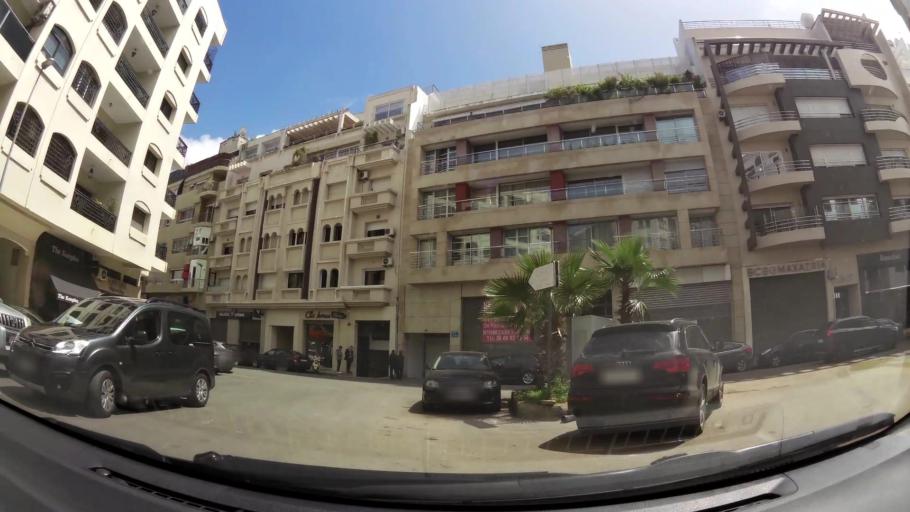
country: MA
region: Grand Casablanca
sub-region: Casablanca
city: Casablanca
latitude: 33.5931
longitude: -7.6419
